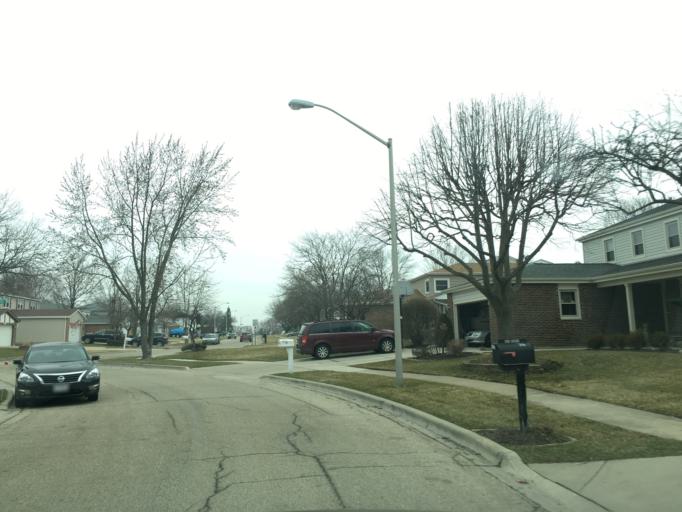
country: US
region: Illinois
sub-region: Cook County
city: Schaumburg
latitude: 42.0385
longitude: -88.1075
